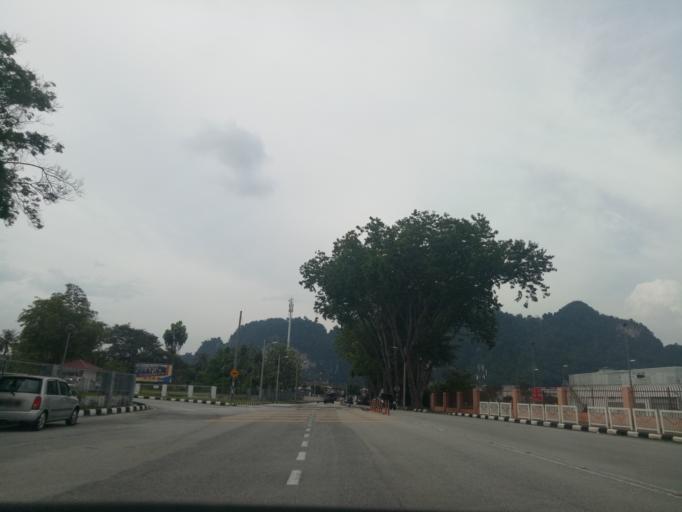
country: MY
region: Perak
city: Ipoh
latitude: 4.5932
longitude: 101.1232
